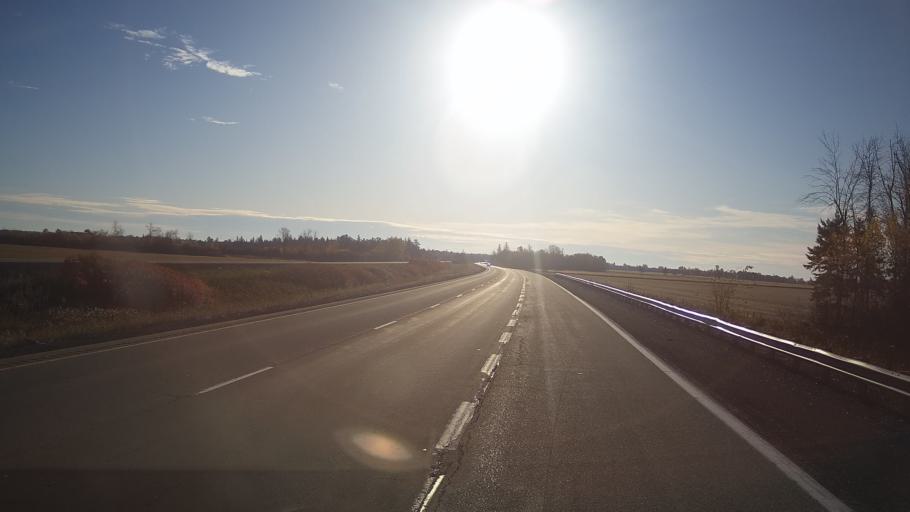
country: CA
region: Ontario
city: Arnprior
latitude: 45.3591
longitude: -76.2289
